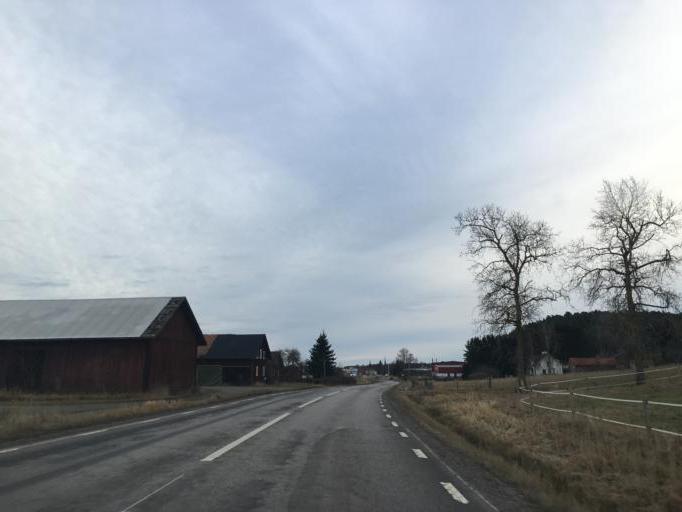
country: SE
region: OEstergoetland
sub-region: Soderkopings Kommun
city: Soederkoeping
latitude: 58.4862
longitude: 16.3007
